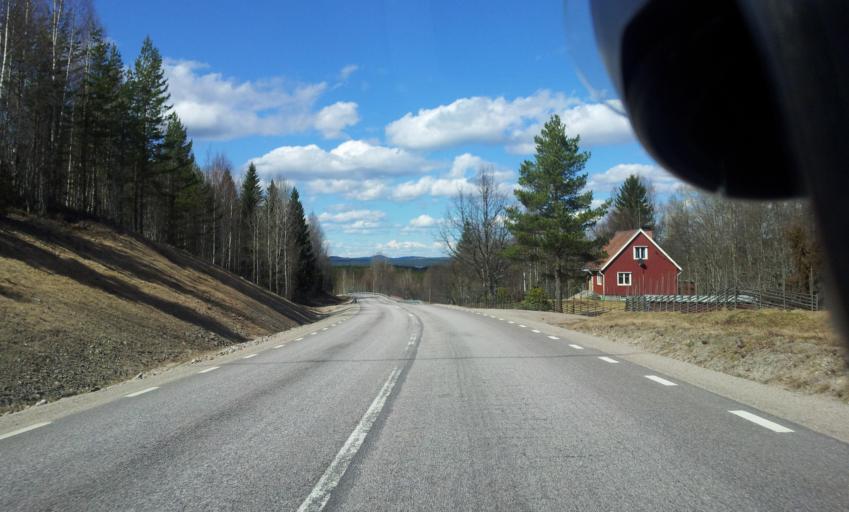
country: SE
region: Gaevleborg
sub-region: Bollnas Kommun
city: Vittsjo
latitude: 61.1518
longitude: 15.8879
